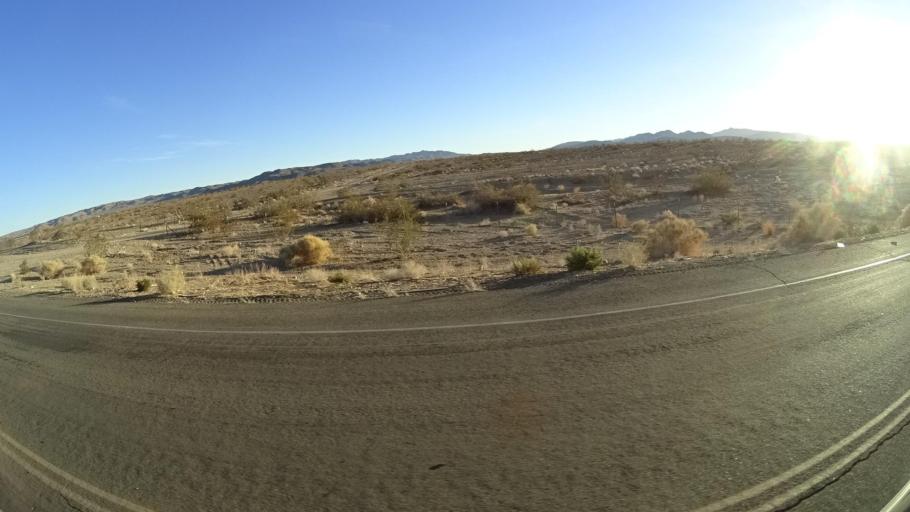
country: US
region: California
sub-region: Kern County
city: Ridgecrest
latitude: 35.6080
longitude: -117.7212
